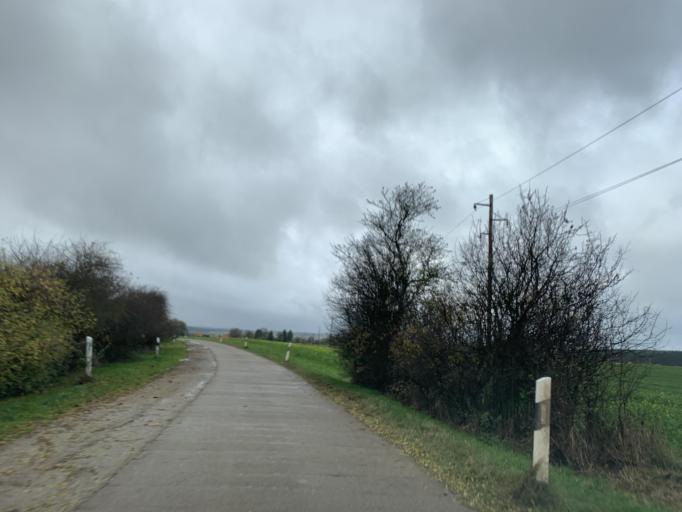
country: DE
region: Mecklenburg-Vorpommern
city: Blankensee
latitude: 53.3799
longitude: 13.2734
